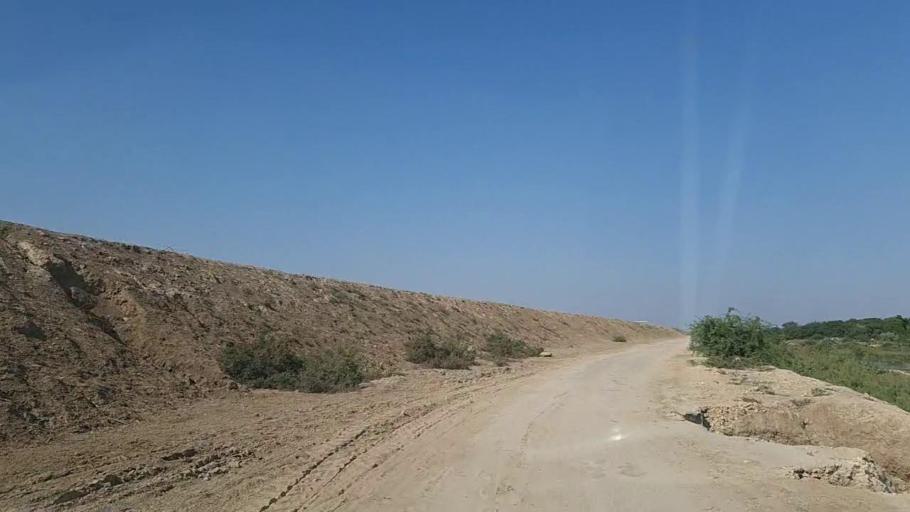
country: PK
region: Sindh
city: Chuhar Jamali
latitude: 24.5680
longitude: 68.0296
